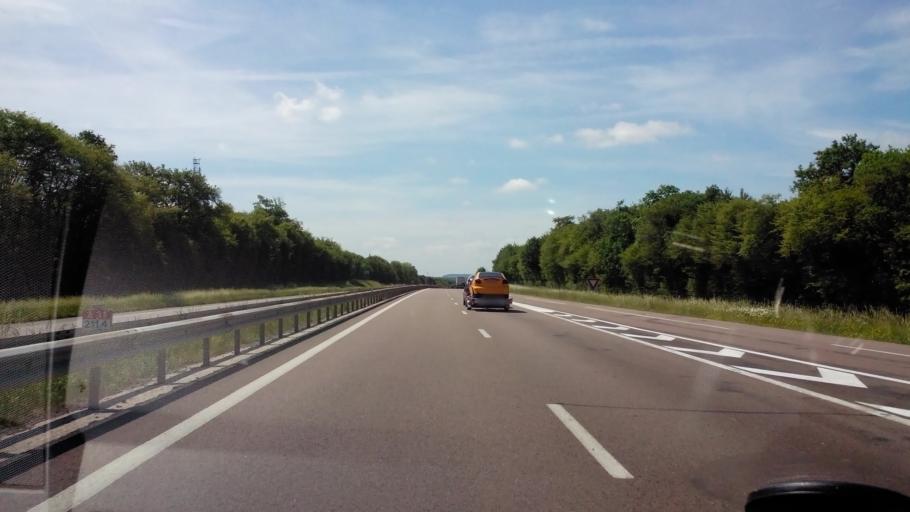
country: FR
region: Lorraine
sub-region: Departement de Meurthe-et-Moselle
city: Colombey-les-Belles
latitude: 48.5079
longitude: 5.9127
